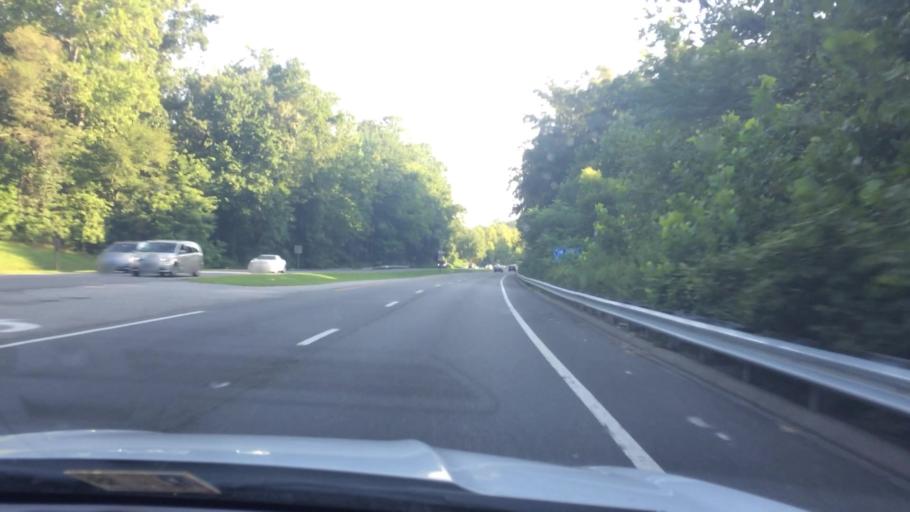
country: US
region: Virginia
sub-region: York County
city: Yorktown
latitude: 37.2294
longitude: -76.5148
